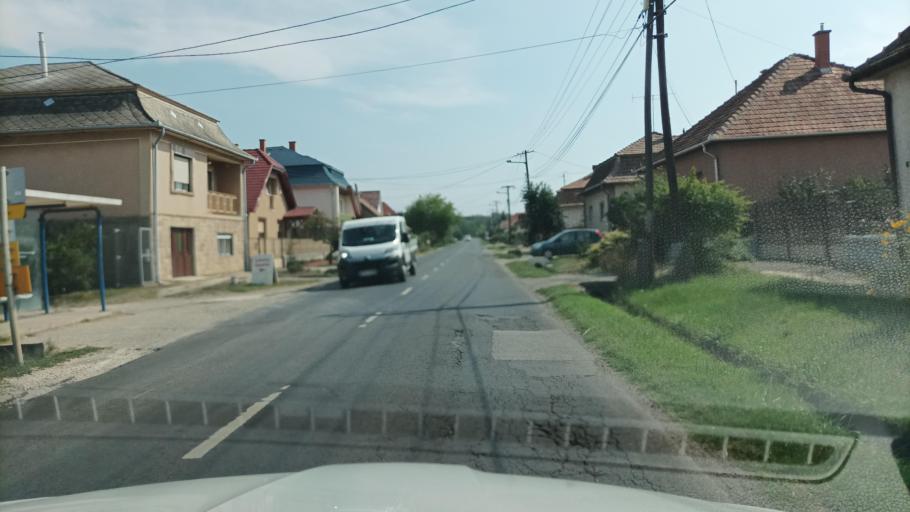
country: HU
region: Pest
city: Hevizgyoerk
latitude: 47.6242
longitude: 19.5309
